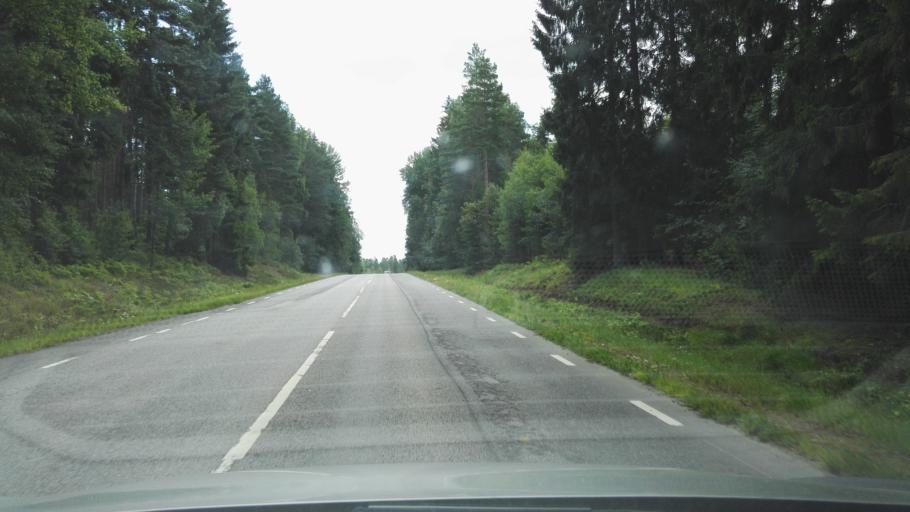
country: SE
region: Kronoberg
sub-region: Vaxjo Kommun
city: Gemla
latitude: 56.8576
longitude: 14.6931
